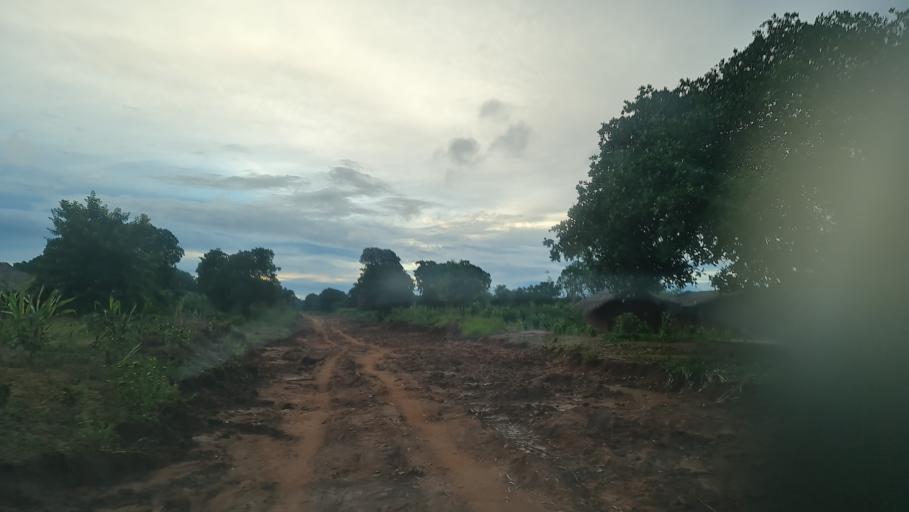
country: MZ
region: Nampula
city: Nacala
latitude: -14.7404
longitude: 39.9422
